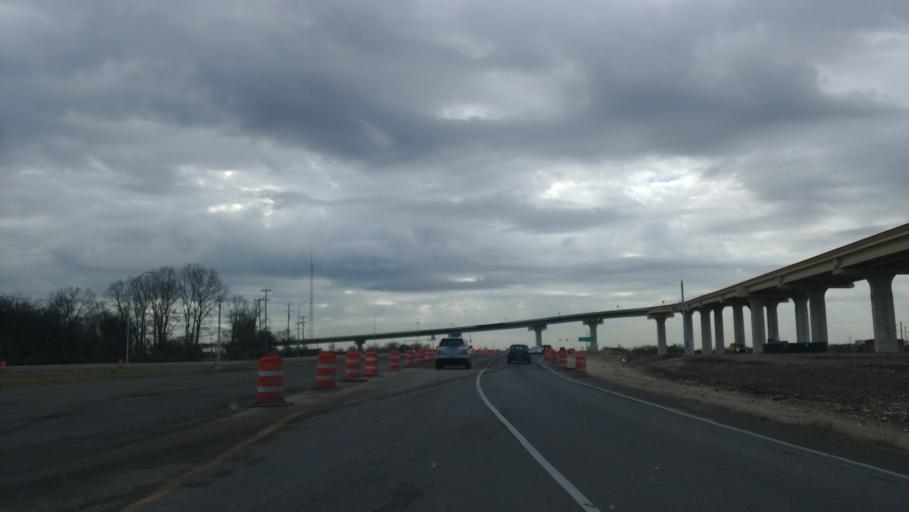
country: US
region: Texas
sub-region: Bexar County
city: Lackland Air Force Base
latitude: 29.3871
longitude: -98.7017
